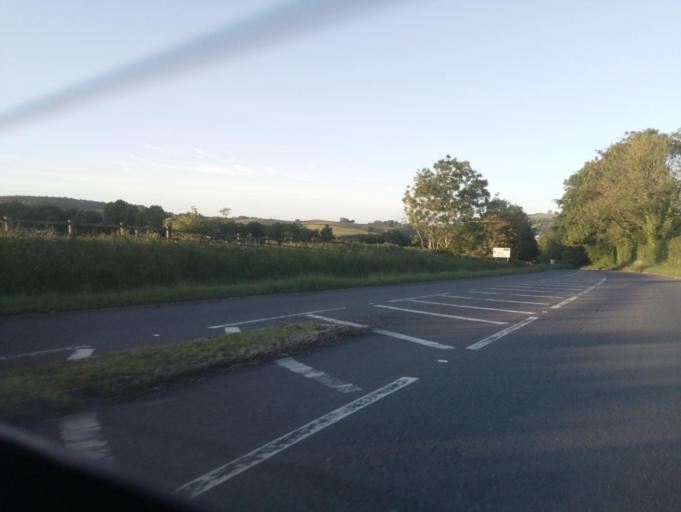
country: GB
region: England
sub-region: Devon
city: Ashburton
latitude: 50.5357
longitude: -3.7105
